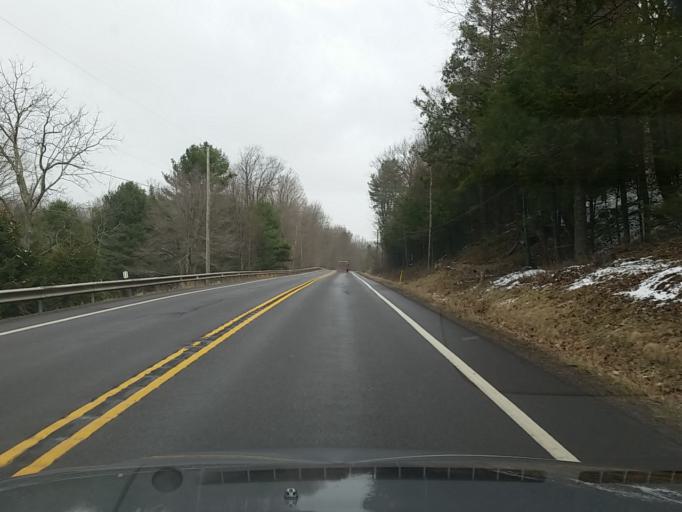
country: US
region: Pennsylvania
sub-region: Sullivan County
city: Laporte
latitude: 41.2890
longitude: -76.3121
